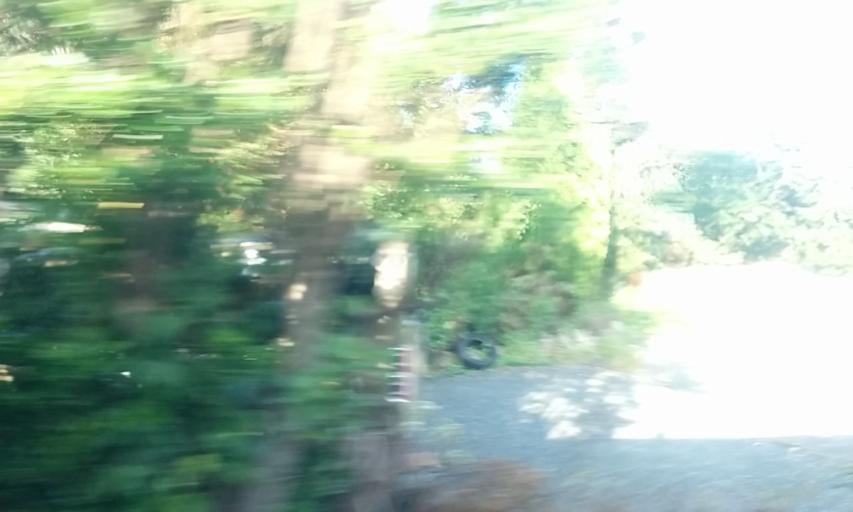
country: JP
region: Kagoshima
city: Nishinoomote
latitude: 30.3803
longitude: 130.6614
